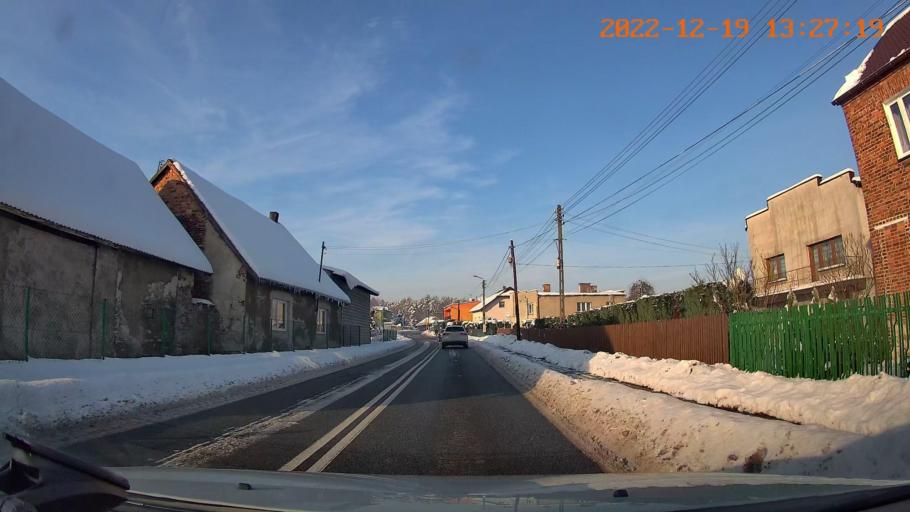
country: PL
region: Silesian Voivodeship
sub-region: Powiat bierunsko-ledzinski
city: Ledziny
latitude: 50.1066
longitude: 19.1368
